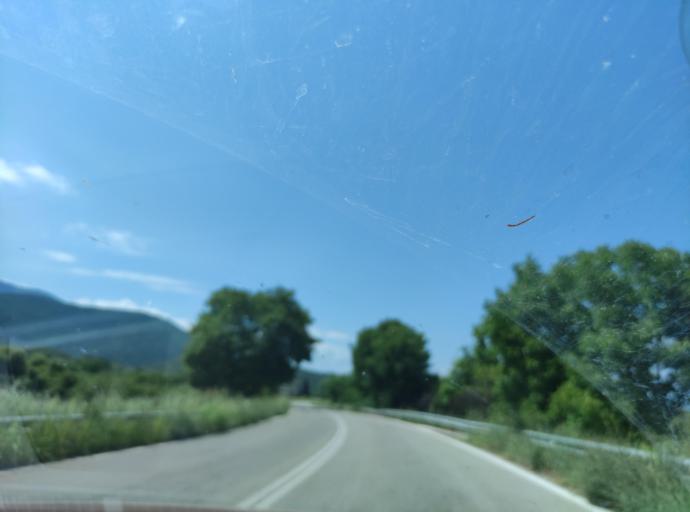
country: GR
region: East Macedonia and Thrace
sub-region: Nomos Kavalas
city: Palaiochori
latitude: 40.9570
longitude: 24.1927
